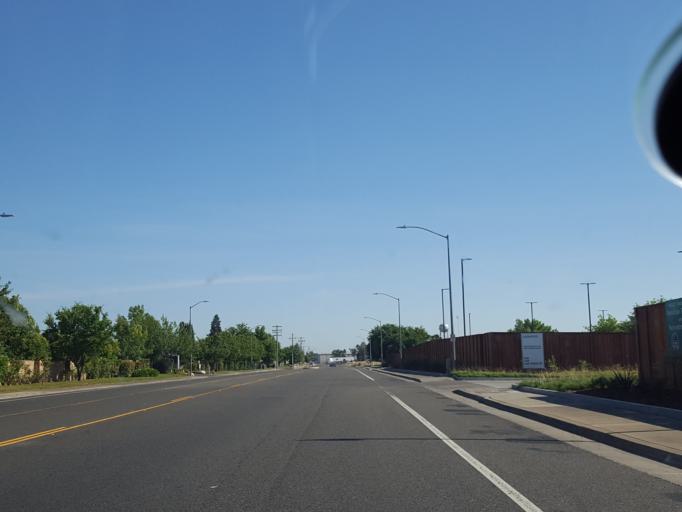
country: US
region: California
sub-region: Sacramento County
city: Florin
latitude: 38.4875
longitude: -121.3905
